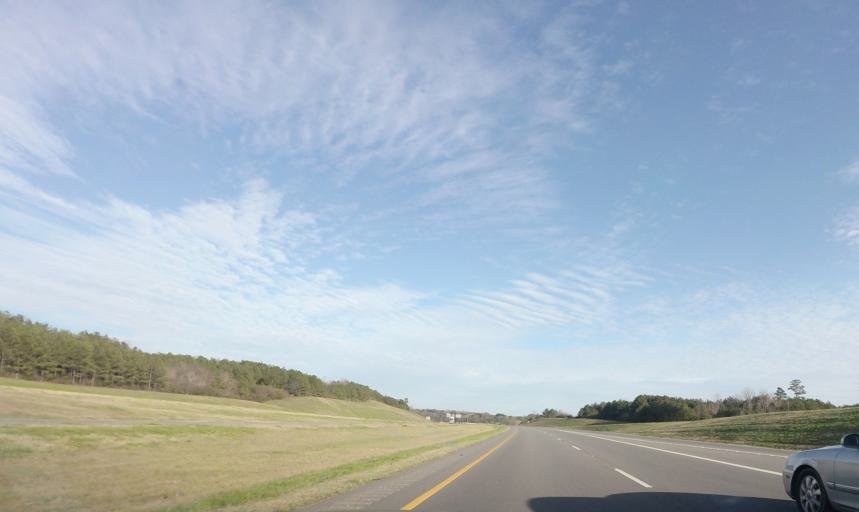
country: US
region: Alabama
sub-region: Walker County
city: Jasper
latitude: 33.8066
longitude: -87.2786
